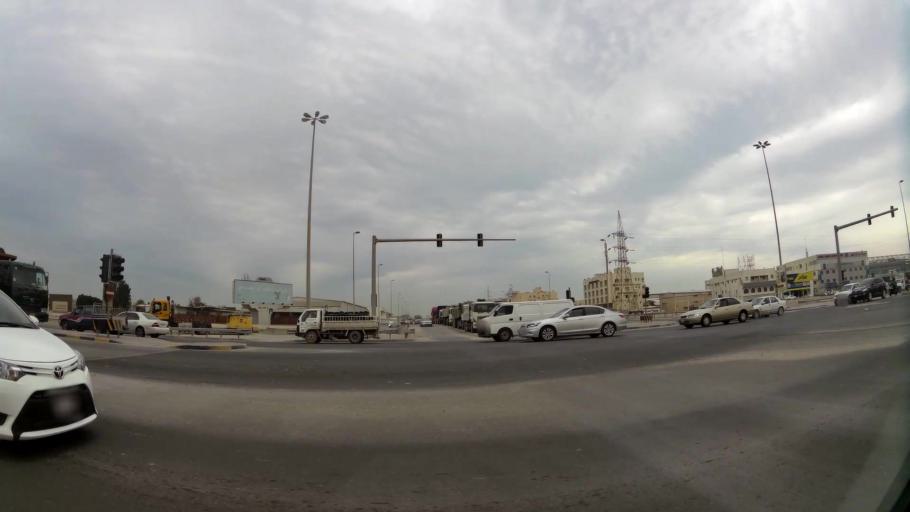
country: BH
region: Northern
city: Sitrah
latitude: 26.1720
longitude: 50.6006
